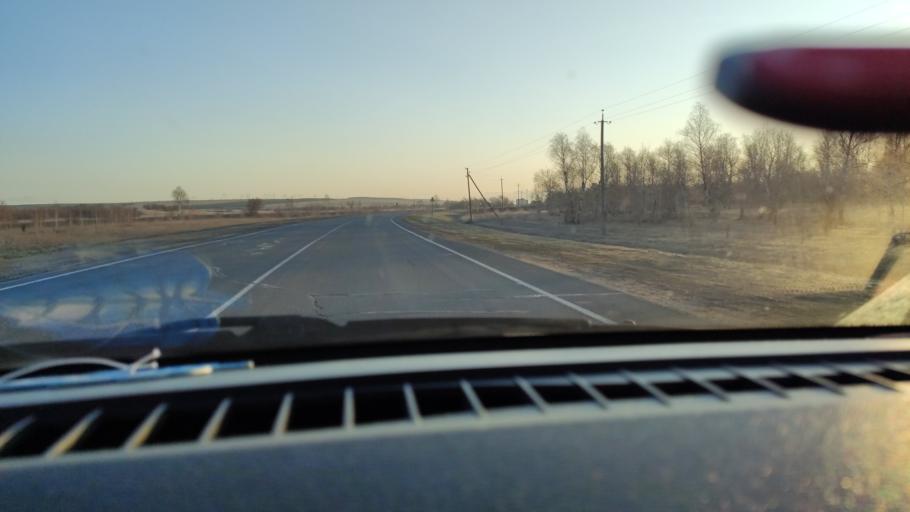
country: RU
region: Saratov
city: Sinodskoye
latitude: 52.0395
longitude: 46.7321
